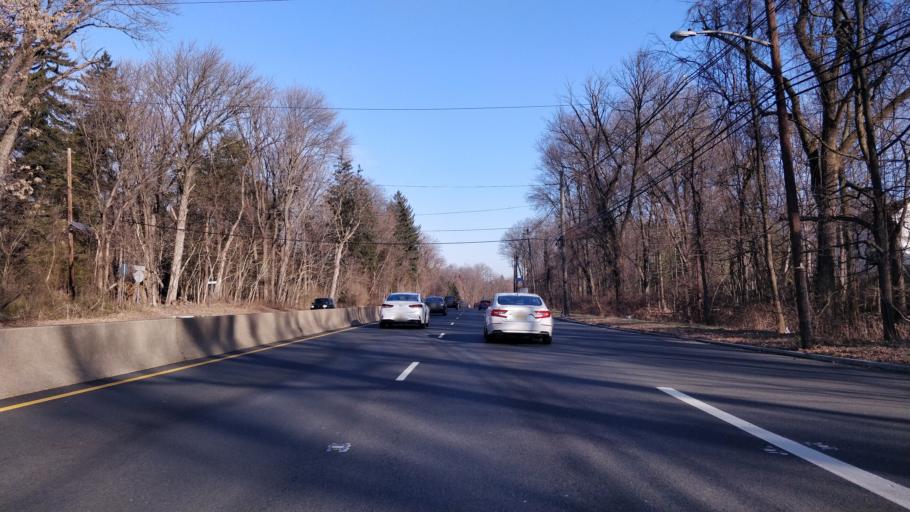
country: US
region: New Jersey
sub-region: Union County
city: Scotch Plains
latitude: 40.6680
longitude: -74.3775
